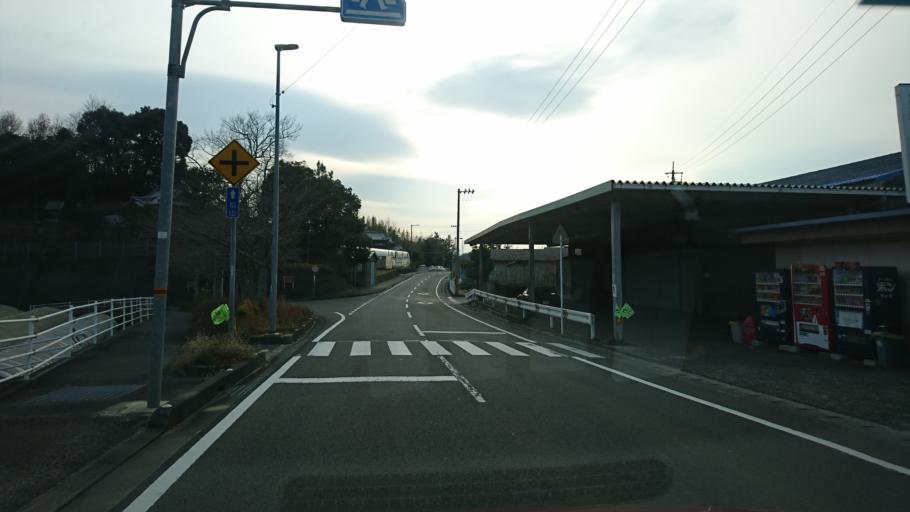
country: JP
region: Ehime
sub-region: Shikoku-chuo Shi
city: Matsuyama
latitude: 33.8915
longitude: 132.8046
